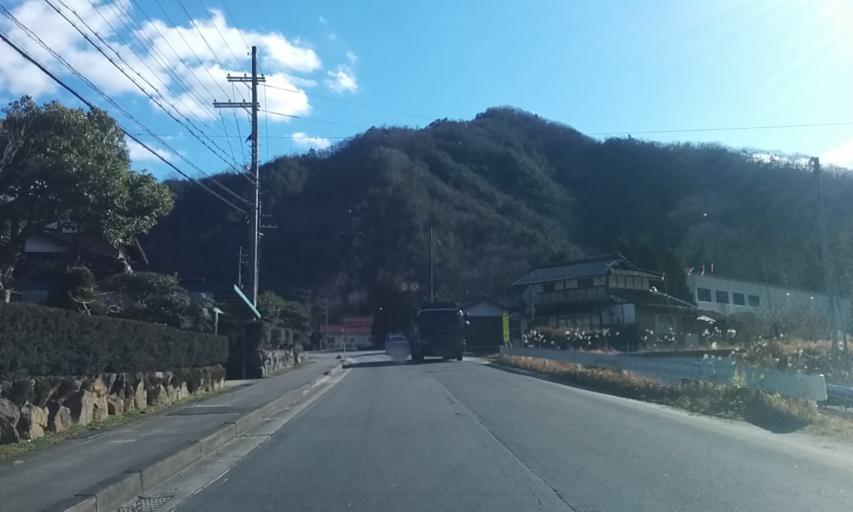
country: JP
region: Hyogo
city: Toyooka
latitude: 35.4632
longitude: 134.9342
